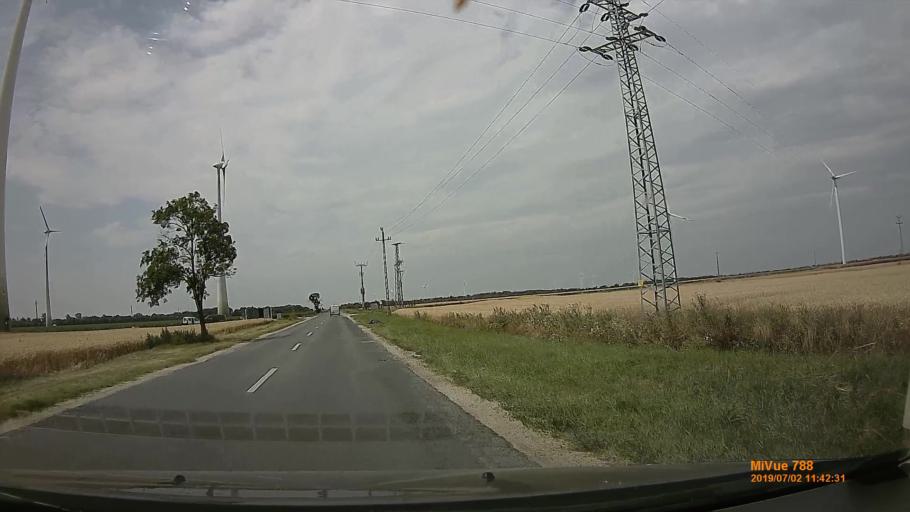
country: HU
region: Gyor-Moson-Sopron
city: Mosonmagyarovar
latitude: 47.8799
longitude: 17.2309
